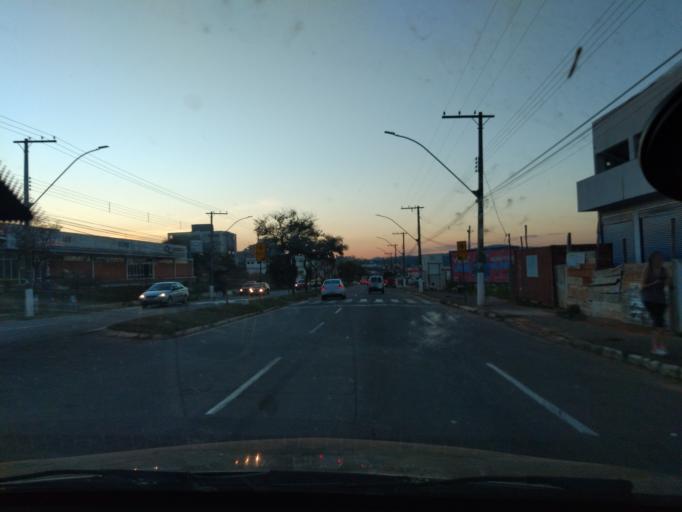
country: BR
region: Minas Gerais
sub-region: Tres Coracoes
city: Tres Coracoes
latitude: -21.6798
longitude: -45.2664
